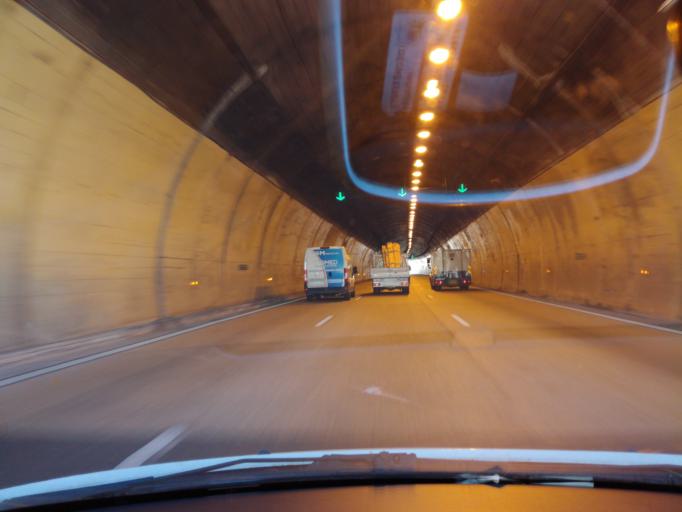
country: FR
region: Provence-Alpes-Cote d'Azur
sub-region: Departement des Alpes-Maritimes
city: Colomars
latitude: 43.7274
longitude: 7.2328
